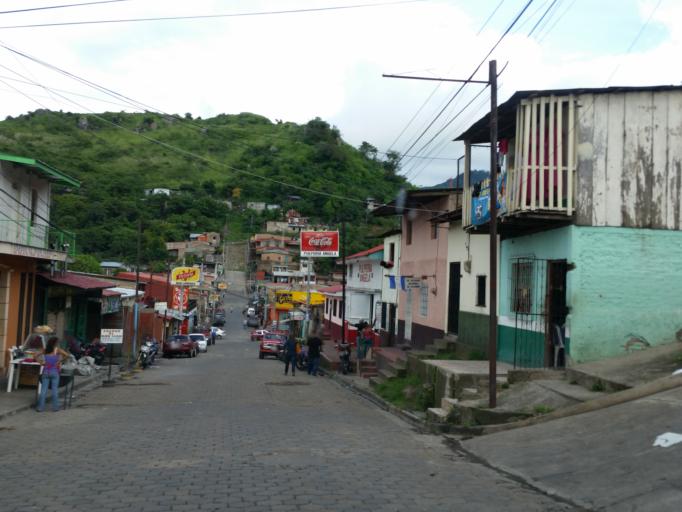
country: NI
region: Matagalpa
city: Matagalpa
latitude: 12.9336
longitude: -85.9132
